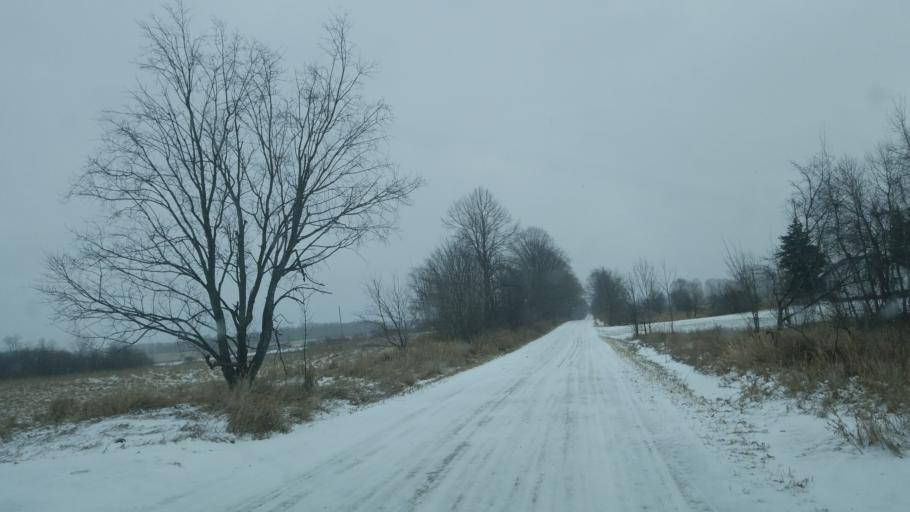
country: US
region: Michigan
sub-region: Osceola County
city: Evart
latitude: 44.0159
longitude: -85.2262
